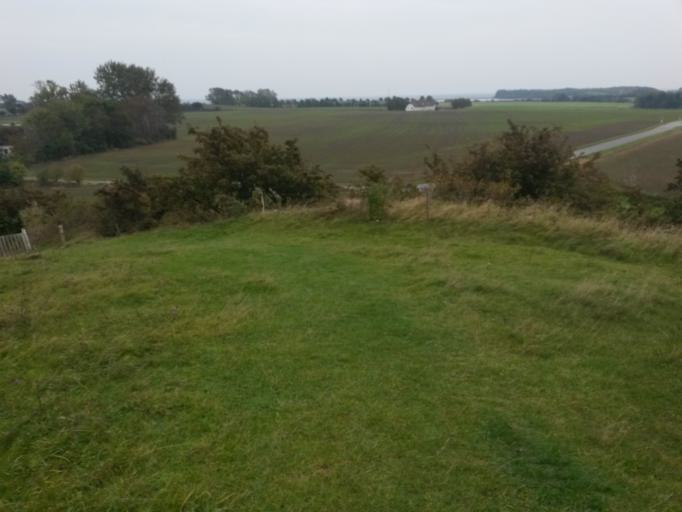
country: DK
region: South Denmark
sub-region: Langeland Kommune
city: Rudkobing
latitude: 54.7390
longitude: 10.7004
